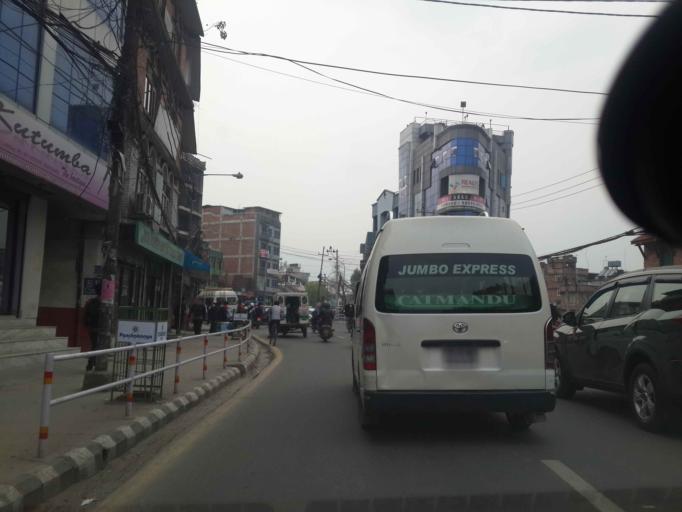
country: NP
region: Central Region
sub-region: Bagmati Zone
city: Patan
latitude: 27.6875
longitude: 85.3167
